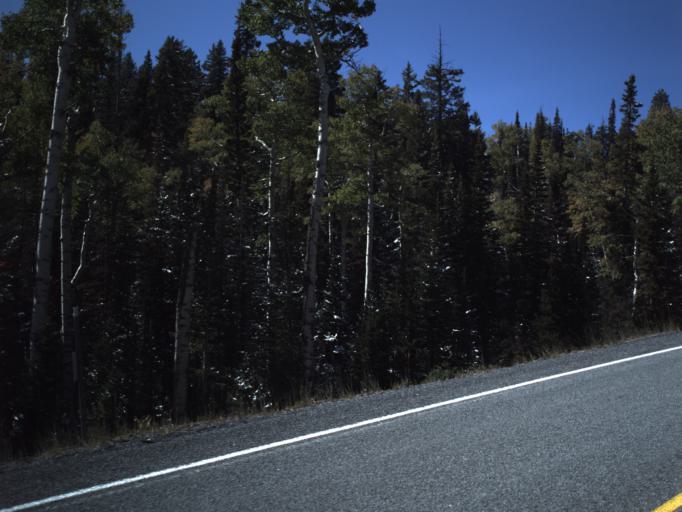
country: US
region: Utah
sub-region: Piute County
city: Junction
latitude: 38.3196
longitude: -112.3705
